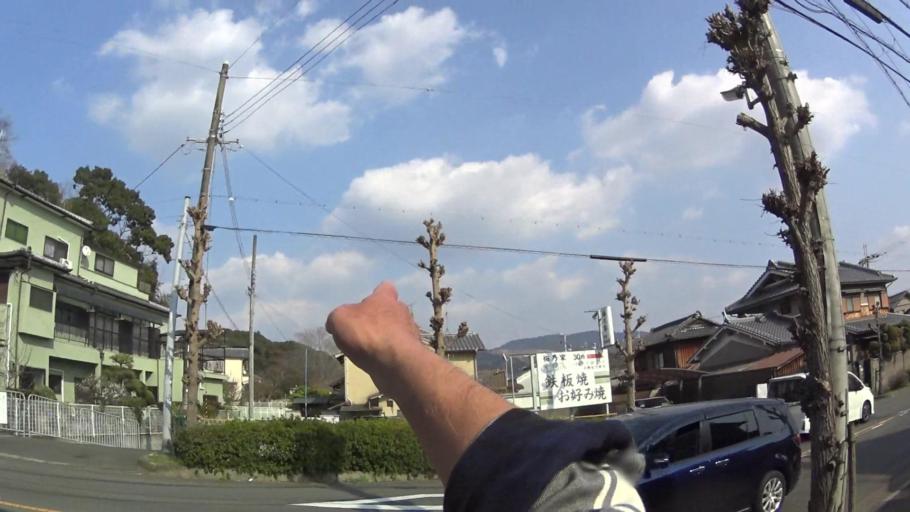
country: JP
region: Nara
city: Nara-shi
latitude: 34.6928
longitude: 135.8258
